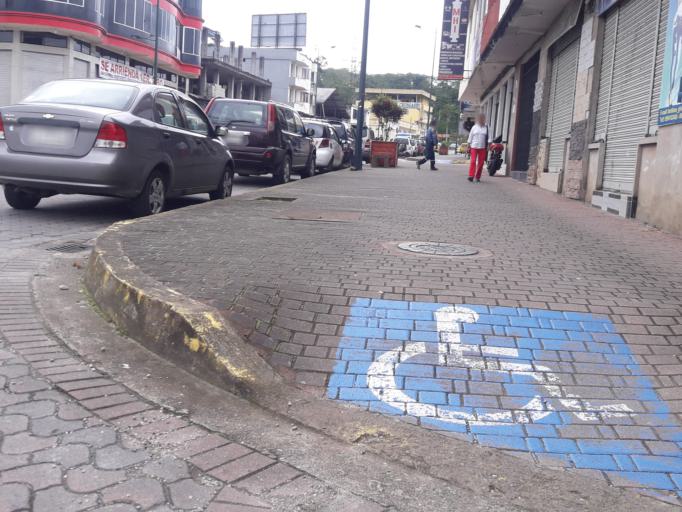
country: EC
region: Napo
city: Tena
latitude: -1.0058
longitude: -77.8101
